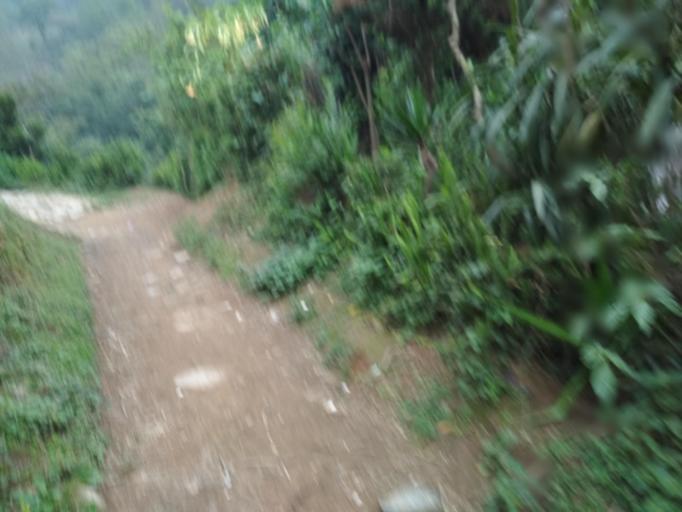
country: MX
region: Veracruz
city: La Perla
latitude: 18.9295
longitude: -97.1511
